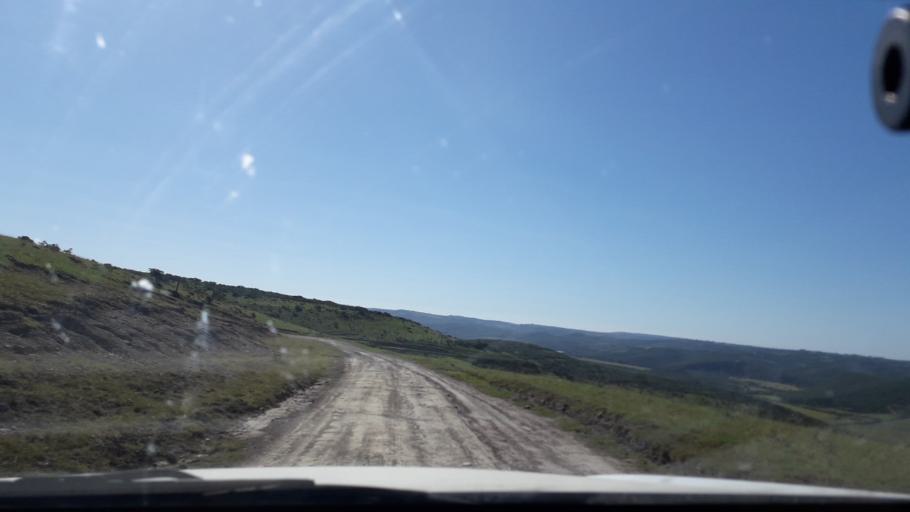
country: ZA
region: Eastern Cape
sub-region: Amathole District Municipality
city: Komga
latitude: -32.7908
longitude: 27.9525
